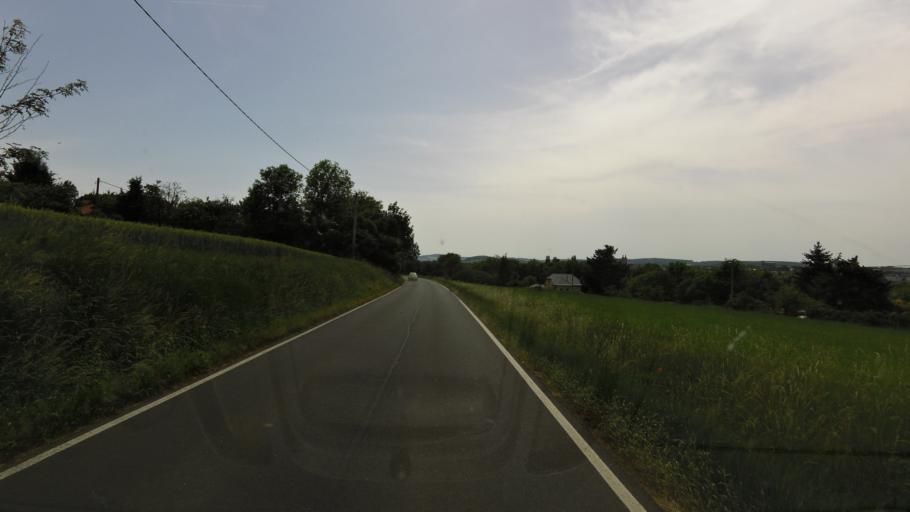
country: CZ
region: Plzensky
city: Prestice
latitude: 49.5771
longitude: 13.3515
